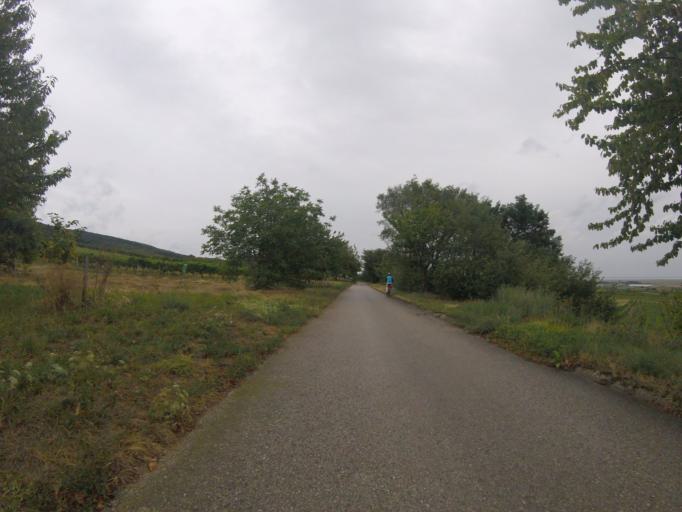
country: AT
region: Burgenland
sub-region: Eisenstadt-Umgebung
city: Donnerskirchen
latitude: 47.9166
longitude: 16.6693
